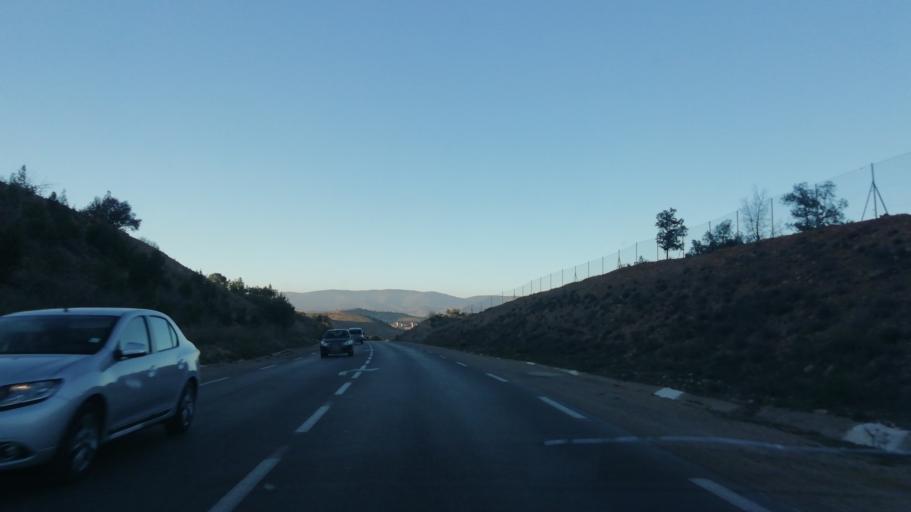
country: DZ
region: Tlemcen
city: Nedroma
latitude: 34.8795
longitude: -1.6689
